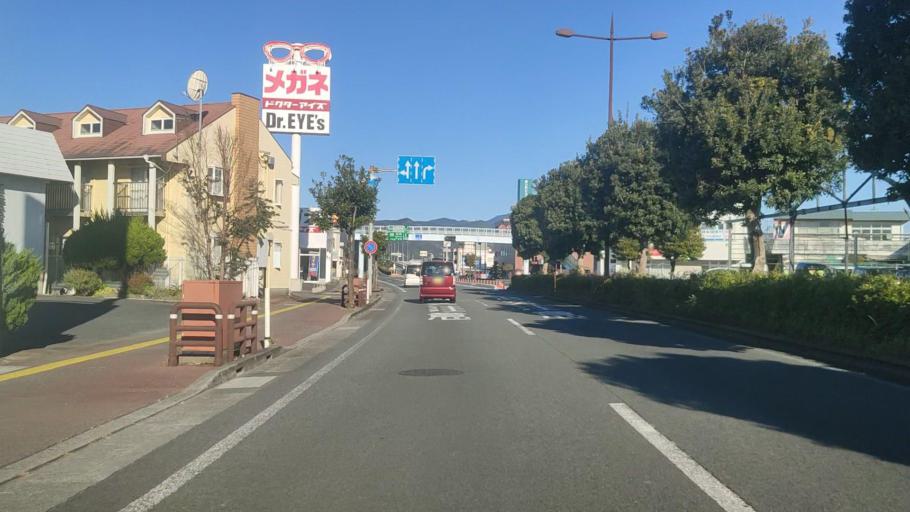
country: JP
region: Miyazaki
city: Nobeoka
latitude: 32.5784
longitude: 131.6832
